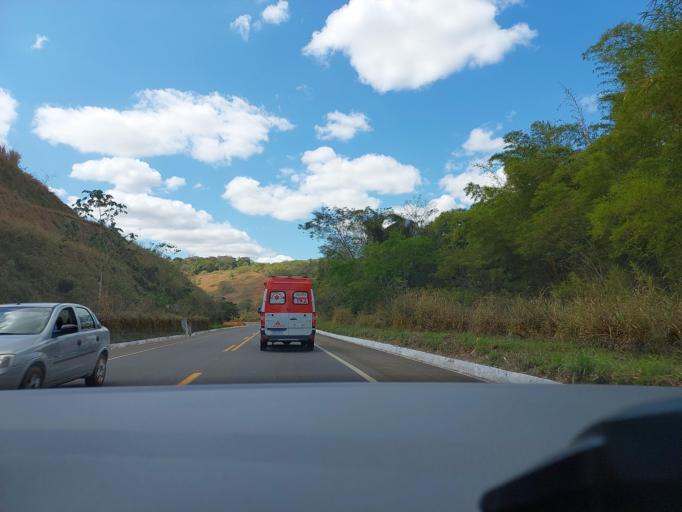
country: BR
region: Minas Gerais
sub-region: Muriae
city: Muriae
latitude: -21.1360
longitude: -42.2986
